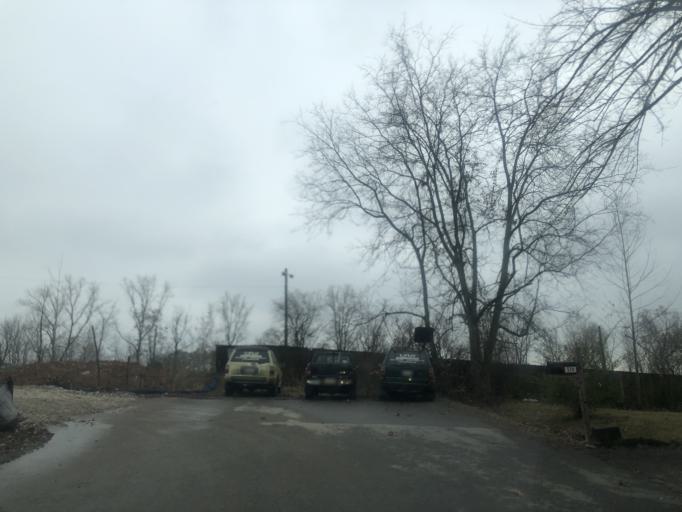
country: US
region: Tennessee
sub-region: Davidson County
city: Lakewood
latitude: 36.1433
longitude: -86.6704
